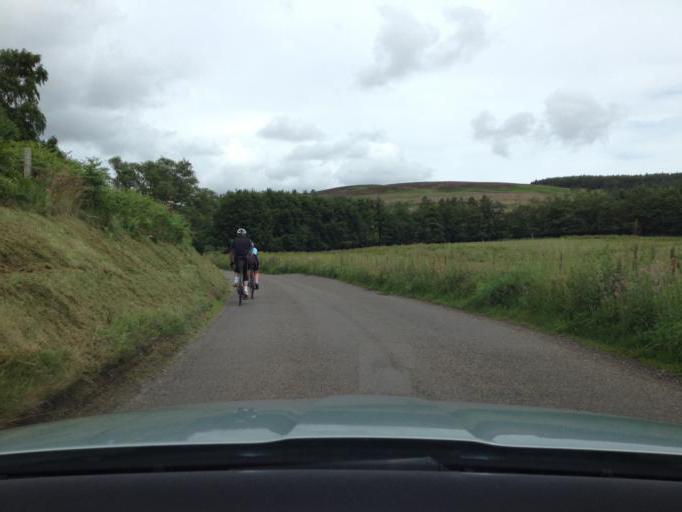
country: GB
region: Scotland
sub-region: Angus
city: Brechin
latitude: 56.8489
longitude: -2.6763
